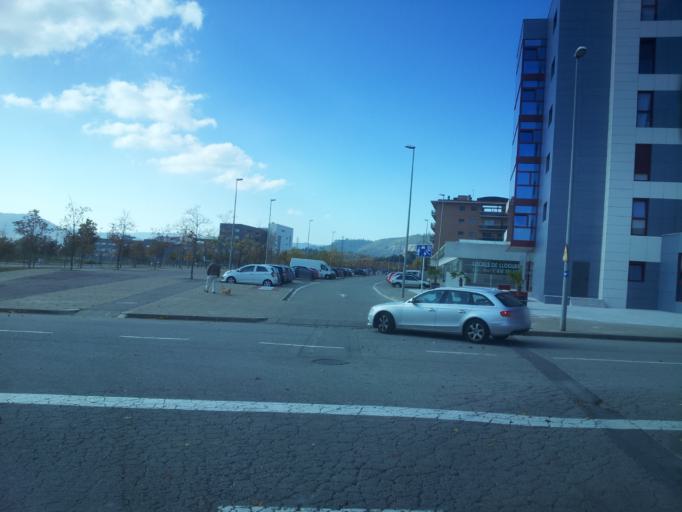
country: ES
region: Catalonia
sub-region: Provincia de Barcelona
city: Vic
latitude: 41.9308
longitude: 2.2433
